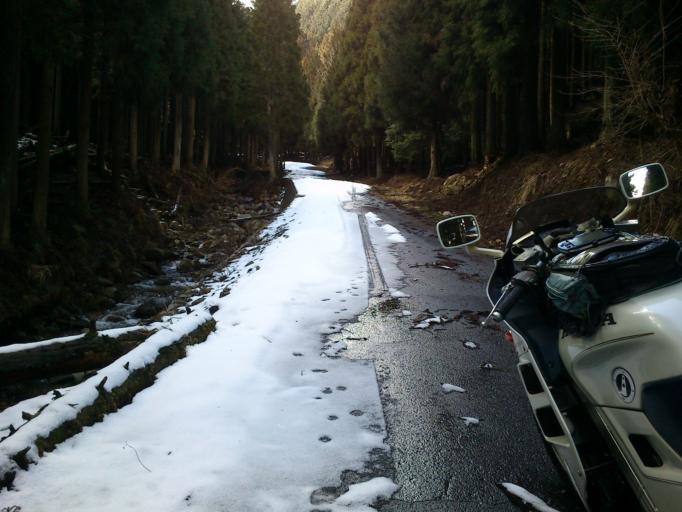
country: JP
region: Kyoto
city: Fukuchiyama
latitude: 35.3834
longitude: 135.0008
